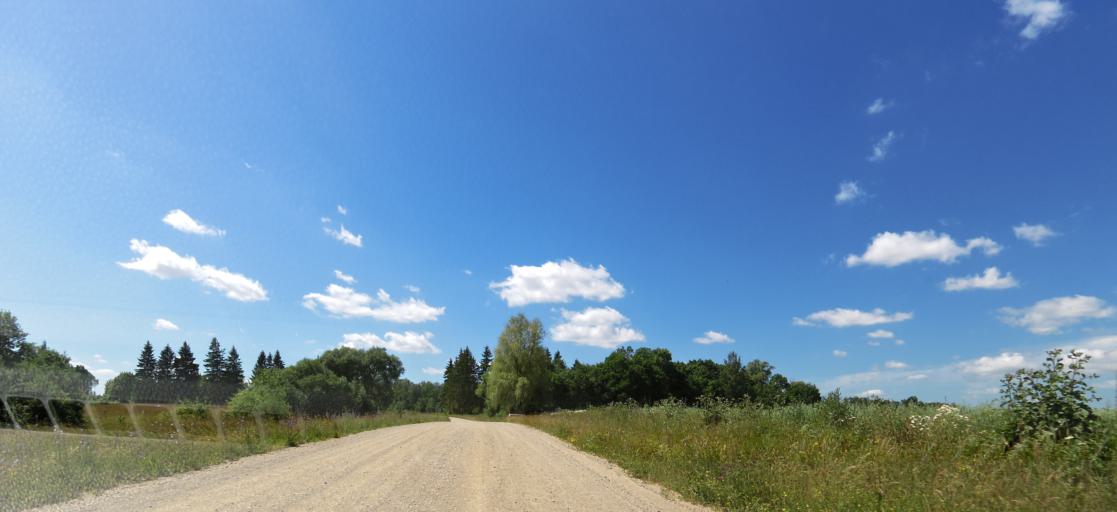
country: LT
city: Kupiskis
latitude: 55.9484
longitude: 24.9748
